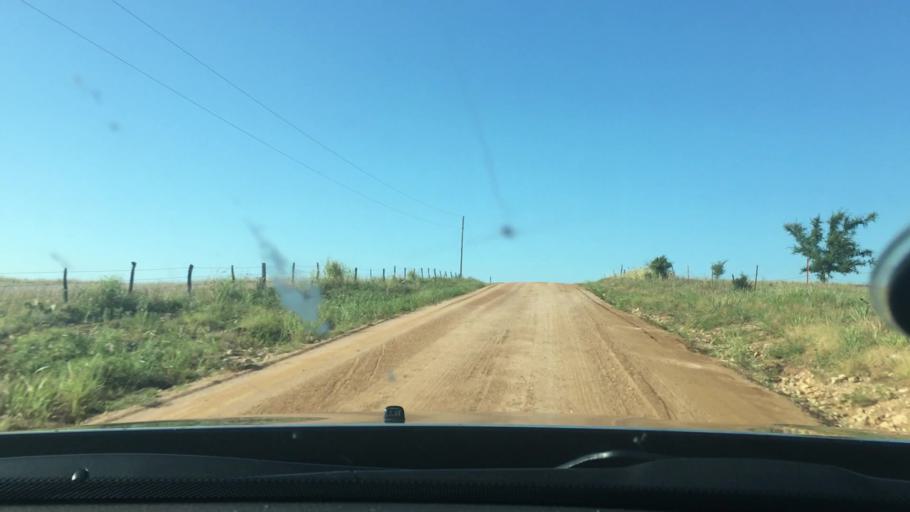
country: US
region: Oklahoma
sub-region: Murray County
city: Sulphur
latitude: 34.4111
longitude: -96.7936
